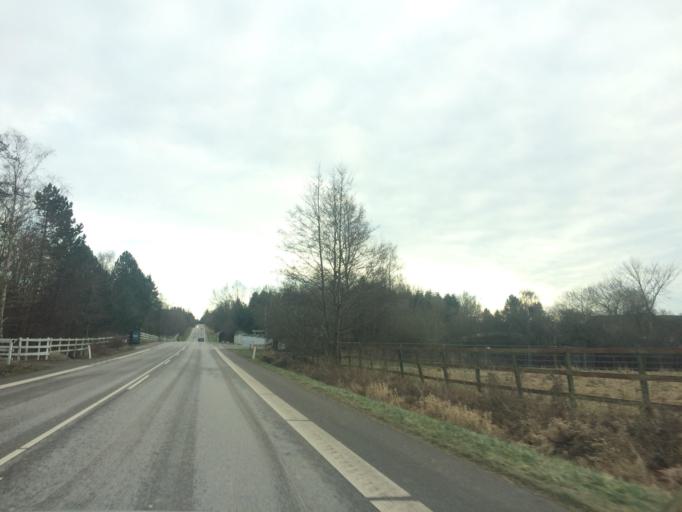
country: DK
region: Capital Region
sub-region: Fredensborg Kommune
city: Fredensborg
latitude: 55.9316
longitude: 12.4381
